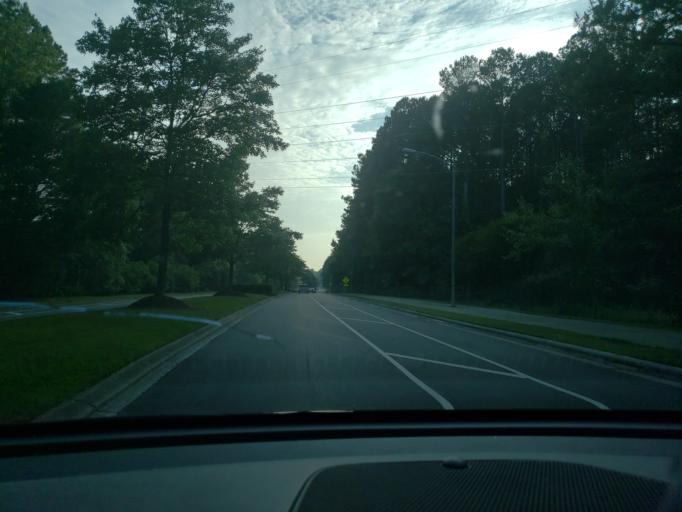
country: US
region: North Carolina
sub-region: Durham County
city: Durham
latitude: 35.9290
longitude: -78.9457
